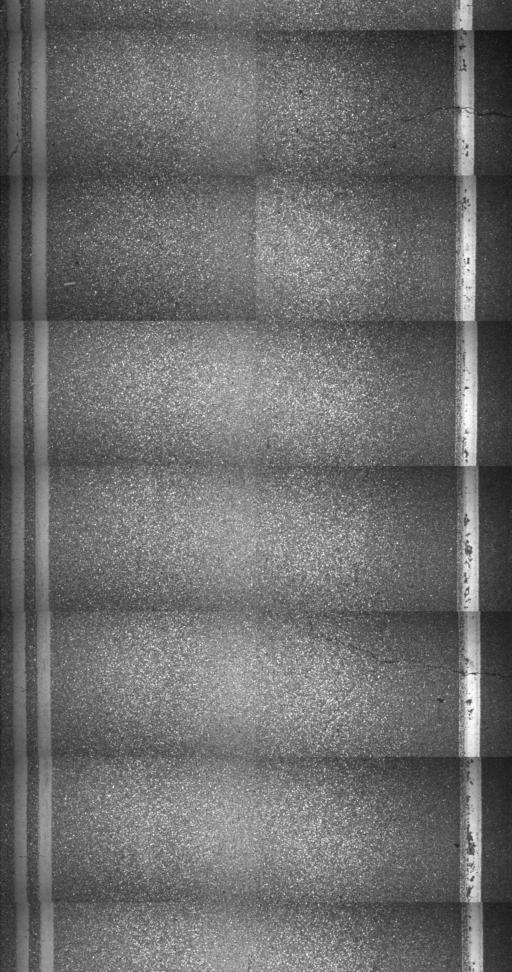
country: US
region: New York
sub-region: Essex County
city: Ticonderoga
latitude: 43.9190
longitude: -73.3126
